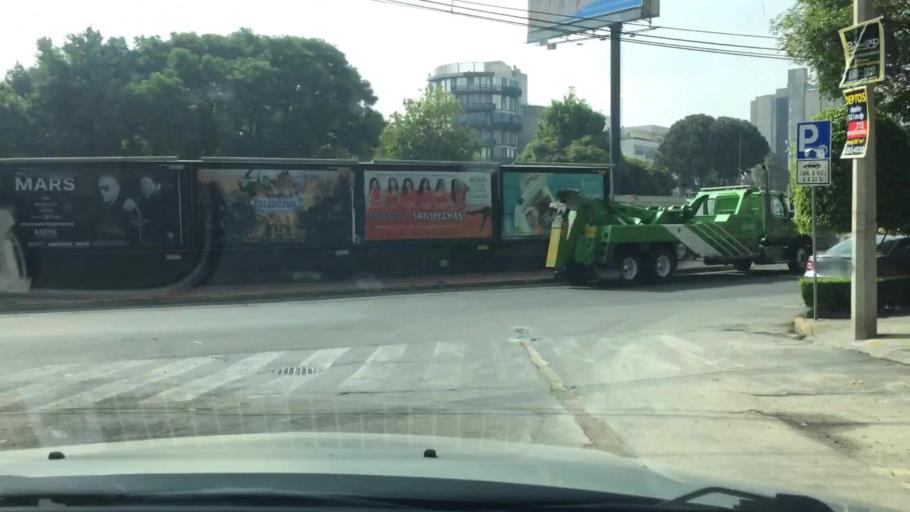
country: MX
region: Mexico City
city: Colonia del Valle
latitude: 19.3843
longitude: -99.1762
